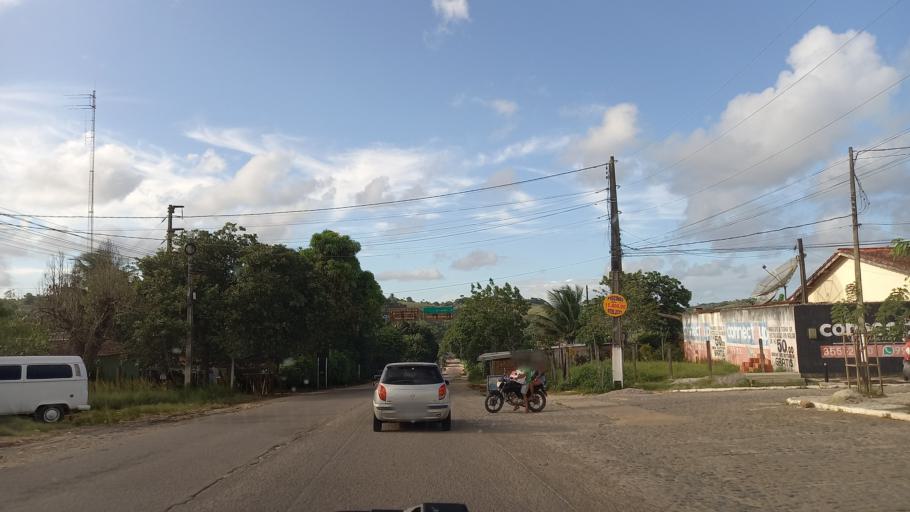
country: BR
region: Pernambuco
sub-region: Rio Formoso
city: Rio Formoso
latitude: -8.6641
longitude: -35.1572
